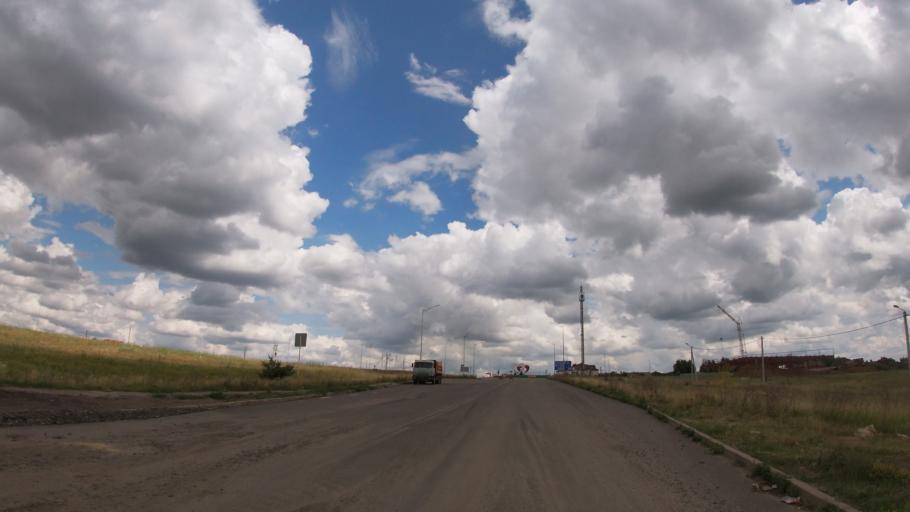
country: RU
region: Belgorod
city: Mayskiy
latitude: 50.5255
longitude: 36.5165
